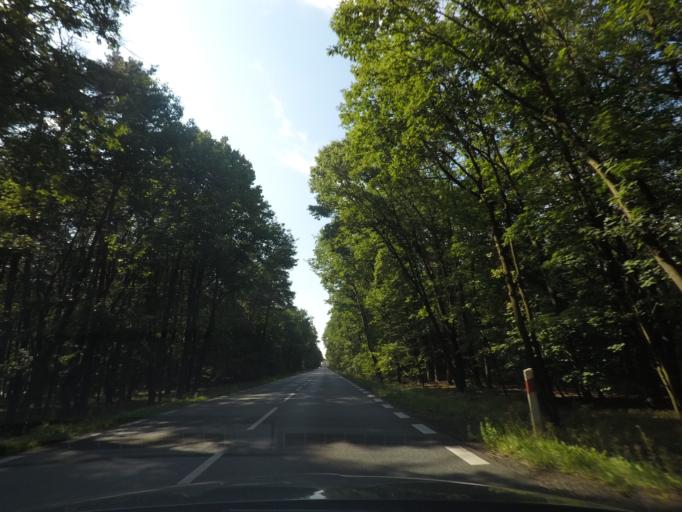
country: PL
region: Silesian Voivodeship
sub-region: Powiat pszczynski
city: Kryry
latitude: 50.0223
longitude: 18.8430
